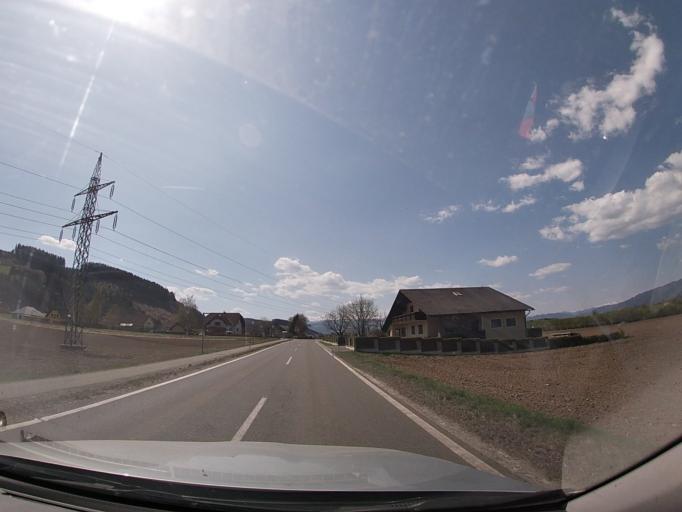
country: AT
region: Styria
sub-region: Politischer Bezirk Murtal
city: Apfelberg
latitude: 47.1910
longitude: 14.8224
